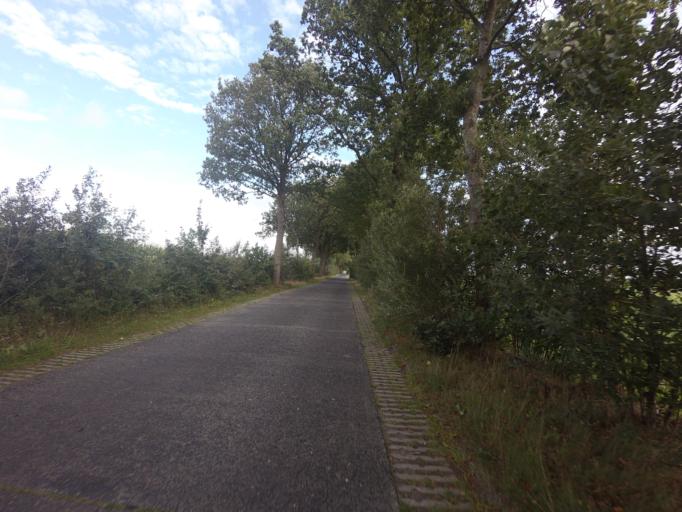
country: NL
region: Friesland
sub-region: Gemeente Heerenveen
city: Jubbega
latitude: 52.9796
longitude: 6.1467
